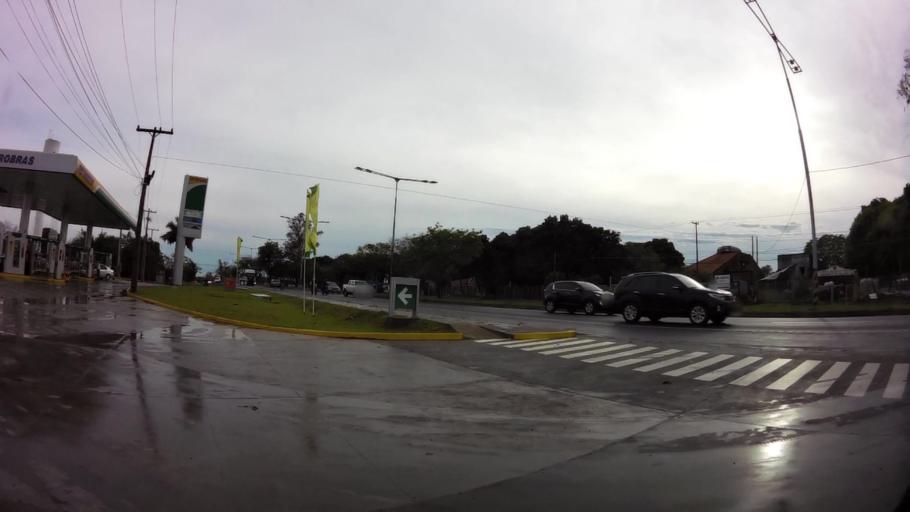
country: PY
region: Central
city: Fernando de la Mora
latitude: -25.2551
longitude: -57.5141
